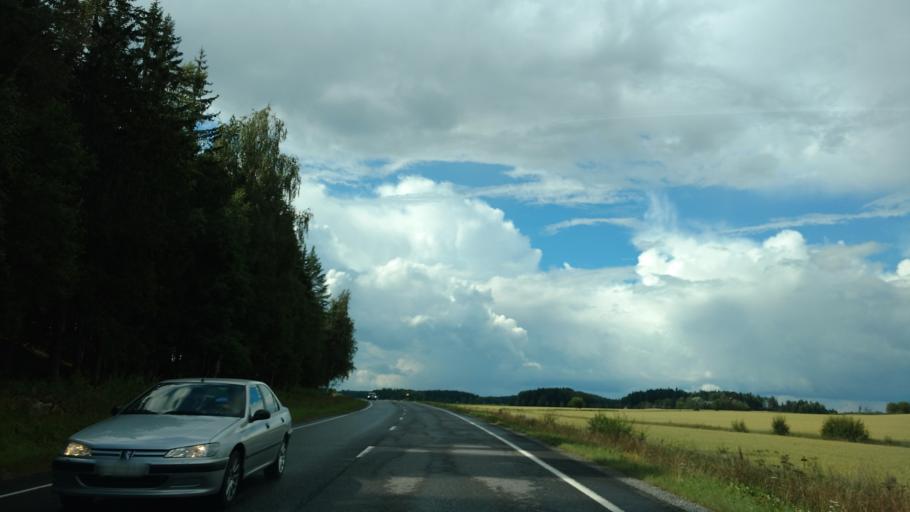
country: FI
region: Varsinais-Suomi
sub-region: Turku
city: Sauvo
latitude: 60.3881
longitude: 22.8788
